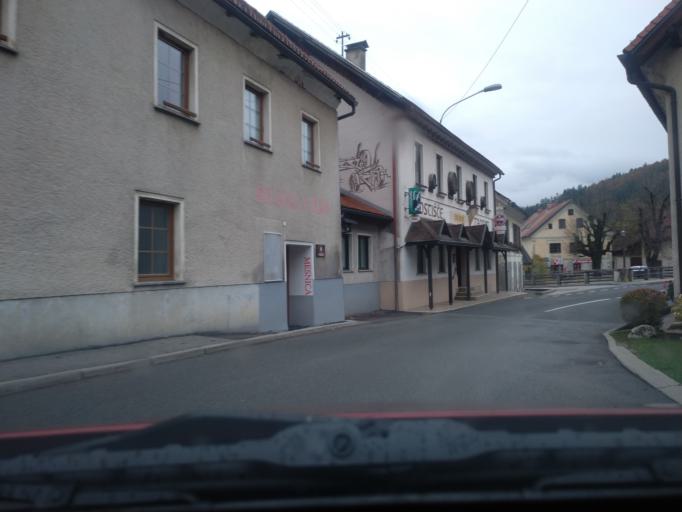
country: SI
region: Gornji Grad
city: Gornji Grad
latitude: 46.2963
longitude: 14.8062
